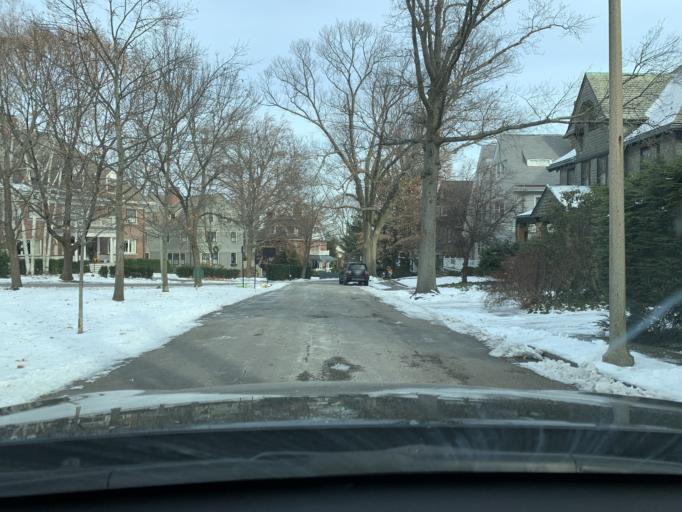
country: US
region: Massachusetts
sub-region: Norfolk County
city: Brookline
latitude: 42.3284
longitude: -71.1202
